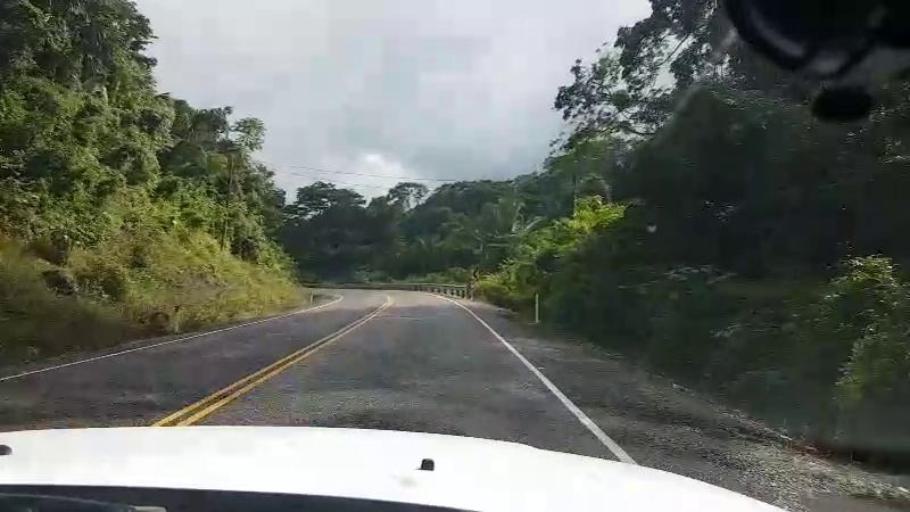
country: BZ
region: Cayo
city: Belmopan
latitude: 17.1569
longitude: -88.6826
